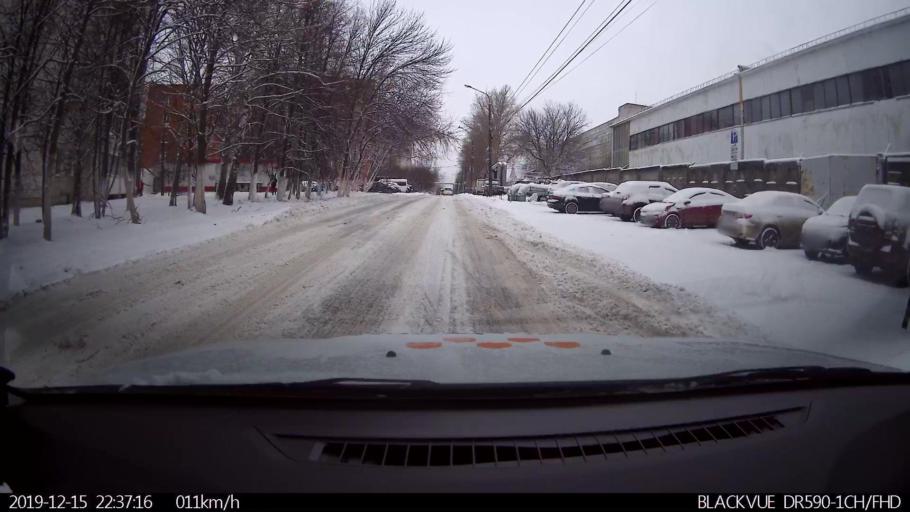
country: RU
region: Nizjnij Novgorod
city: Nizhniy Novgorod
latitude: 56.2386
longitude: 43.9711
